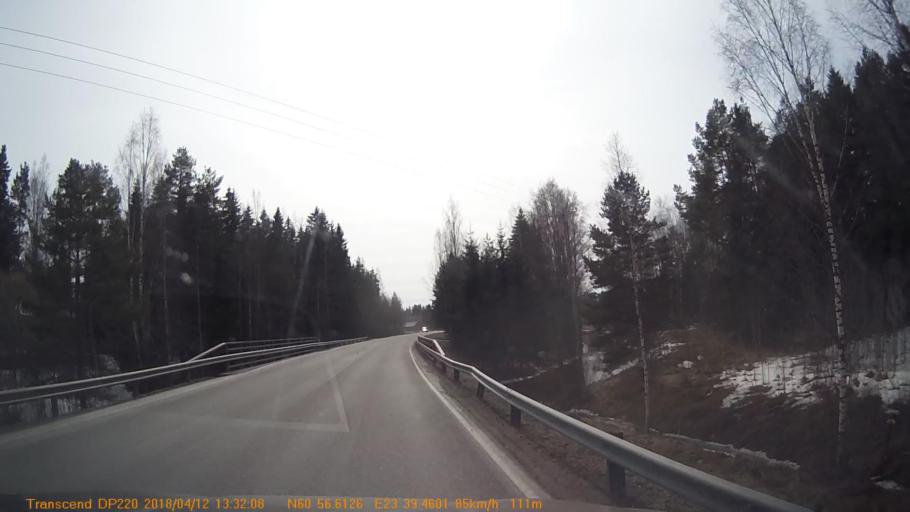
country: FI
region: Haeme
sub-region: Forssa
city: Forssa
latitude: 60.9433
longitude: 23.6575
